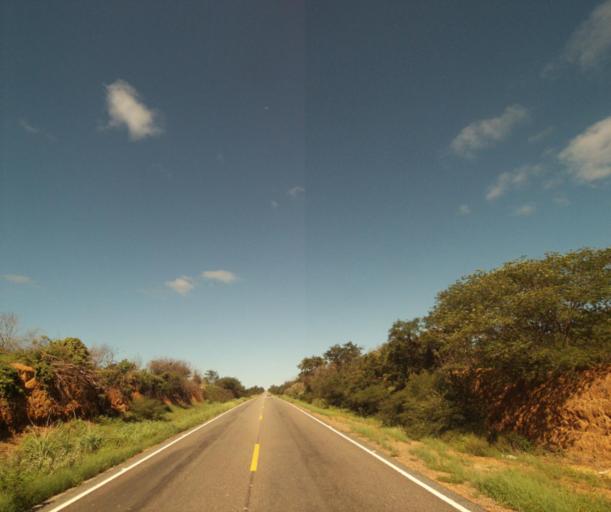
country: BR
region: Bahia
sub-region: Palmas De Monte Alto
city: Palmas de Monte Alto
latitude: -14.2444
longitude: -43.0986
